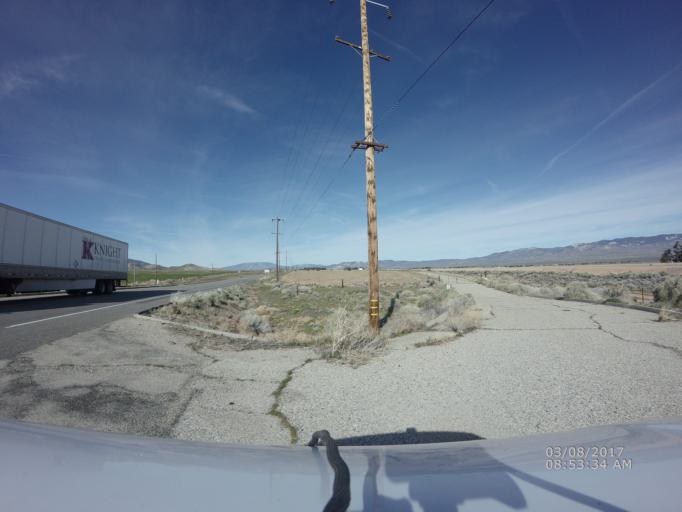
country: US
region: California
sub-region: Los Angeles County
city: Green Valley
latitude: 34.7747
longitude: -118.5627
